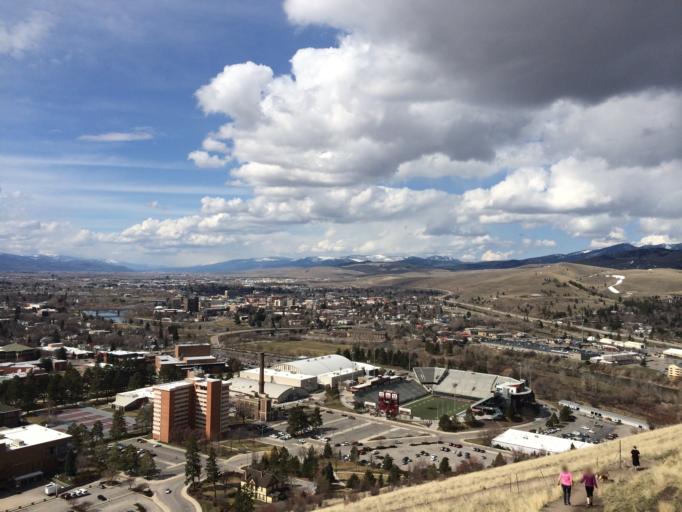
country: US
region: Montana
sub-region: Missoula County
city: Missoula
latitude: 46.8596
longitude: -113.9785
